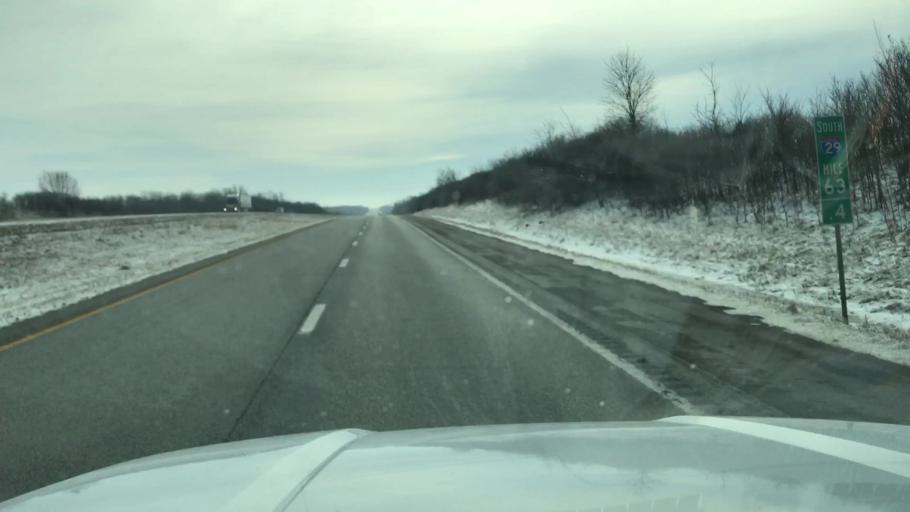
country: US
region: Missouri
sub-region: Andrew County
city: Savannah
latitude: 39.9491
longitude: -94.9482
